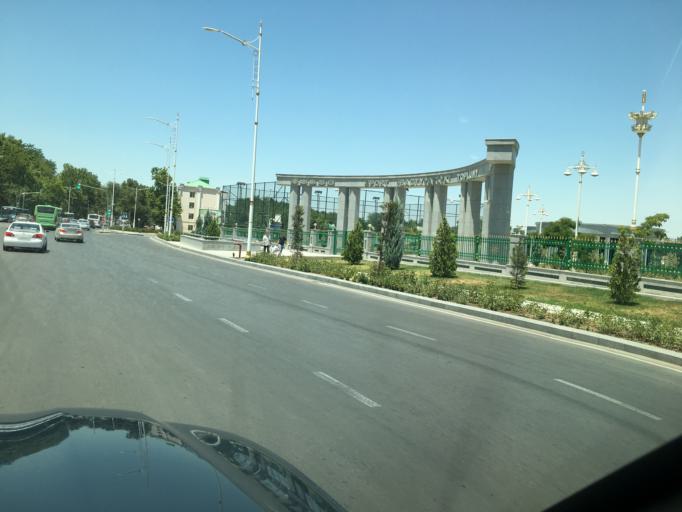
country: TM
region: Ahal
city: Ashgabat
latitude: 37.9431
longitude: 58.3615
